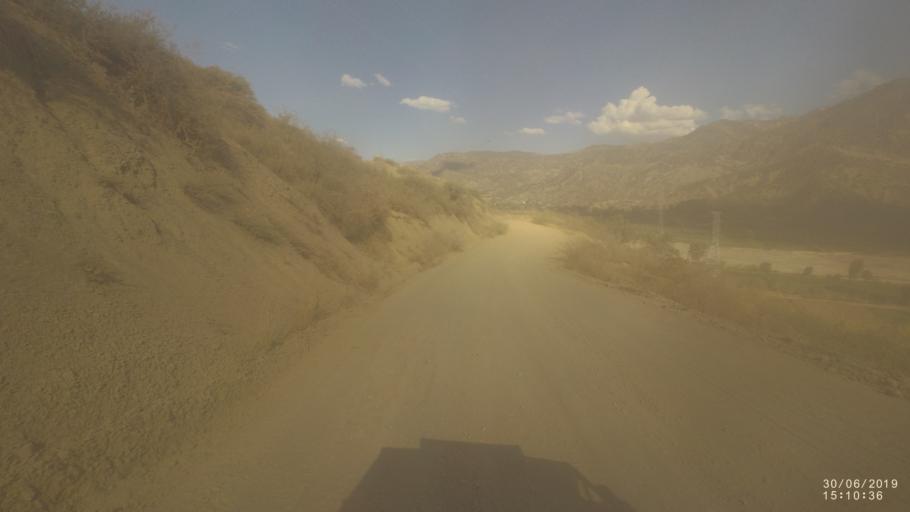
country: BO
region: Cochabamba
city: Irpa Irpa
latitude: -17.7301
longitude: -66.2946
